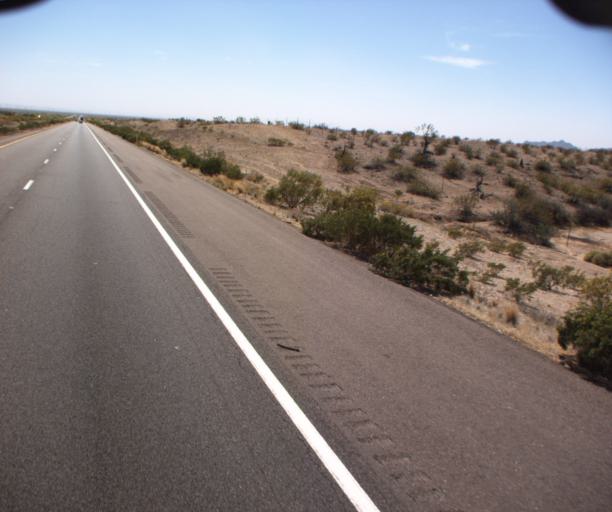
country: US
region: Arizona
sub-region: Maricopa County
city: Gila Bend
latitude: 33.0930
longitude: -112.6488
